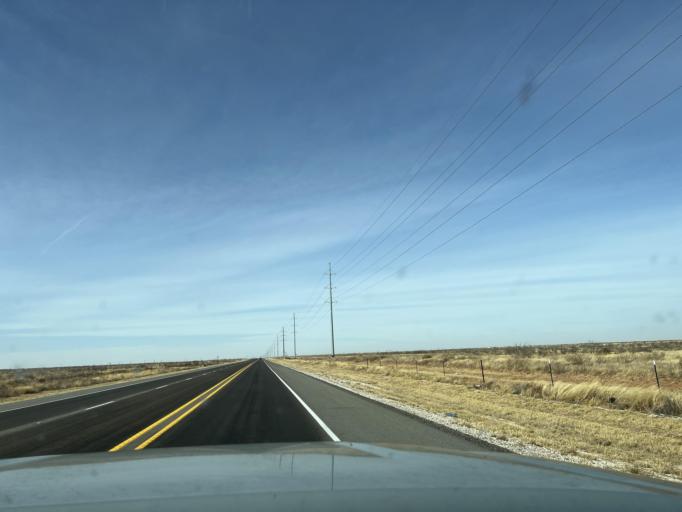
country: US
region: Texas
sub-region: Andrews County
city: Andrews
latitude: 32.3405
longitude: -102.6884
